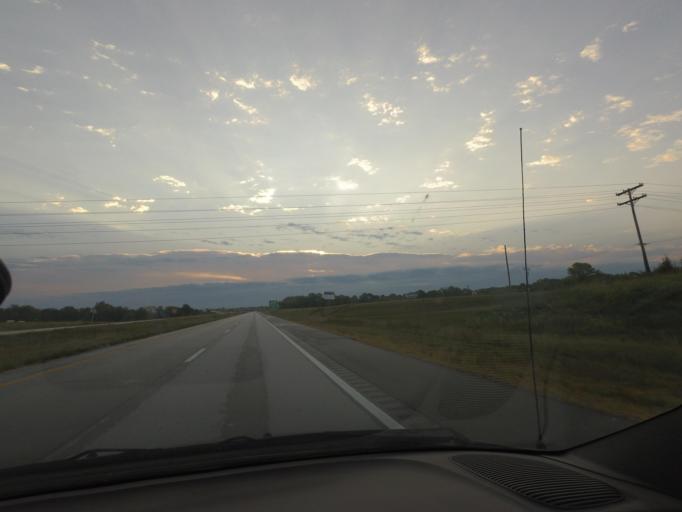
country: US
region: Missouri
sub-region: Macon County
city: Macon
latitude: 39.7509
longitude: -92.2683
